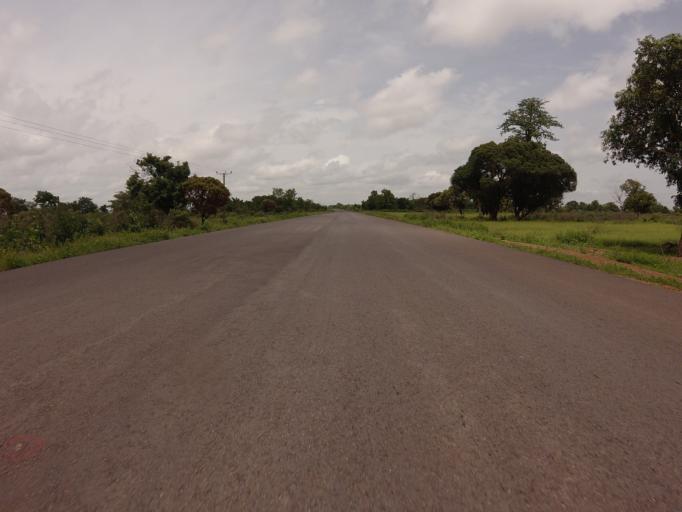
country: GH
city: Kpandae
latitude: 8.5204
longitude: 0.2812
